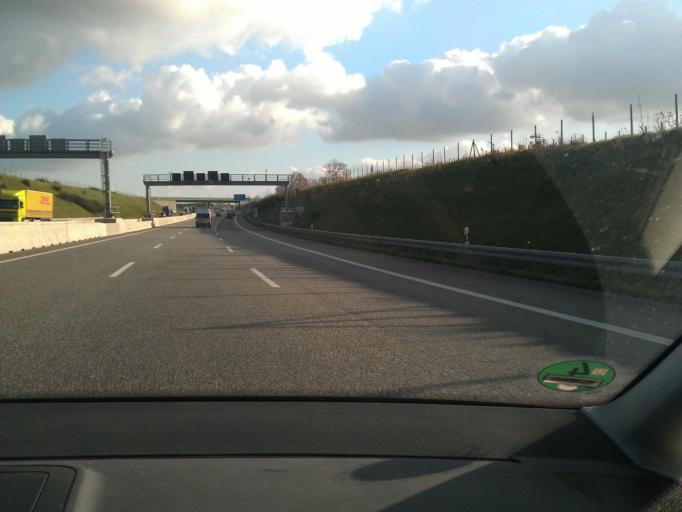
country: DE
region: North Rhine-Westphalia
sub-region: Regierungsbezirk Koln
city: Merzenich
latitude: 50.8503
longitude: 6.5090
